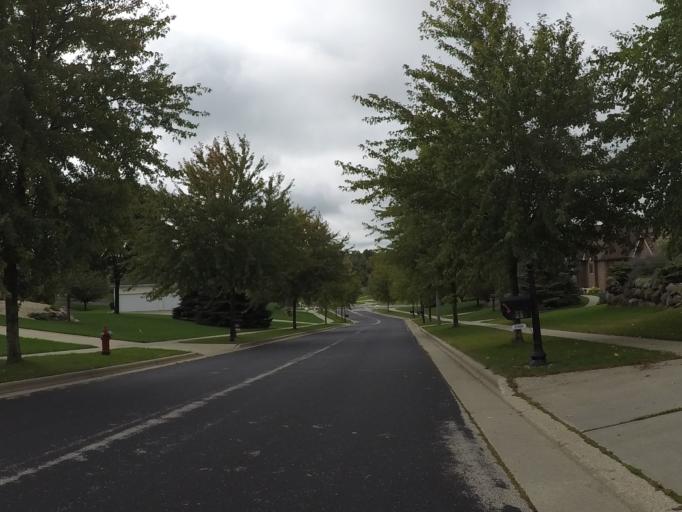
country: US
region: Wisconsin
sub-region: Dane County
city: Verona
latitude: 43.0411
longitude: -89.5477
